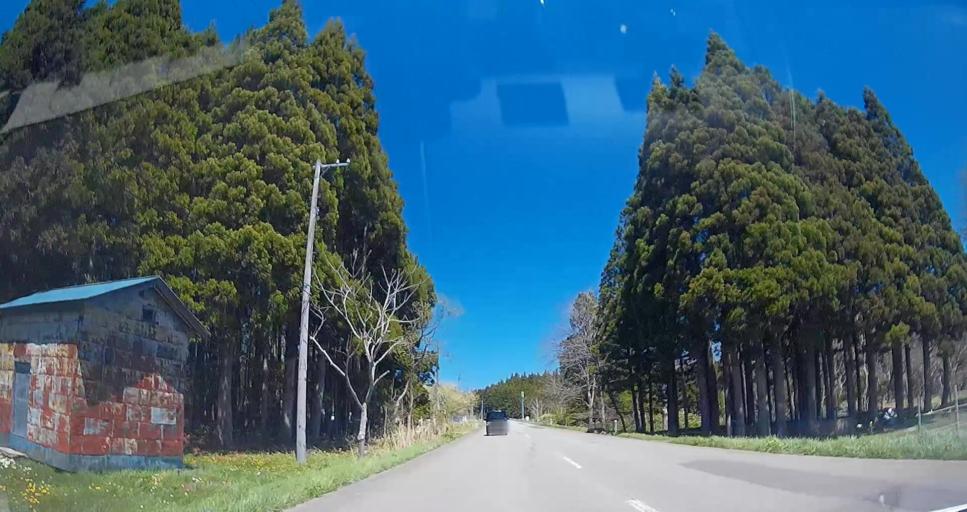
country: JP
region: Aomori
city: Mutsu
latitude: 41.2932
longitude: 141.3953
